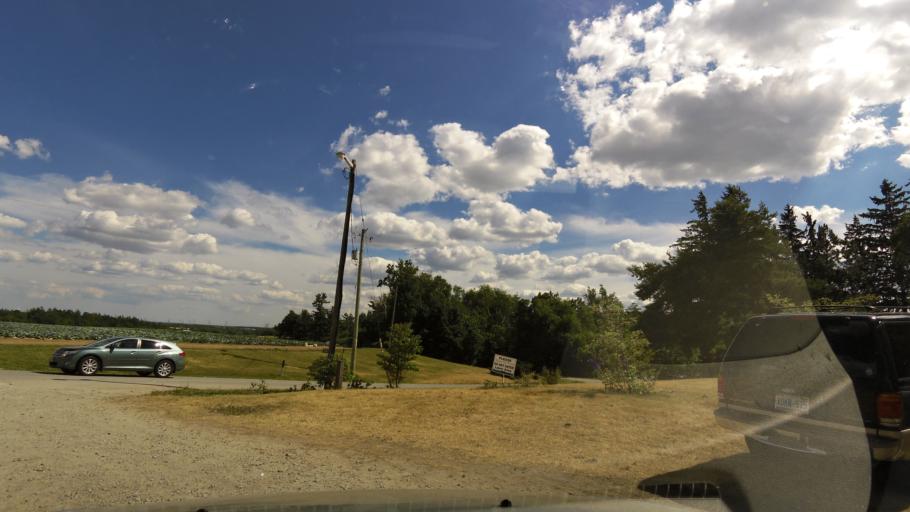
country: CA
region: Ontario
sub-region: Halton
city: Milton
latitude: 43.5734
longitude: -79.9338
